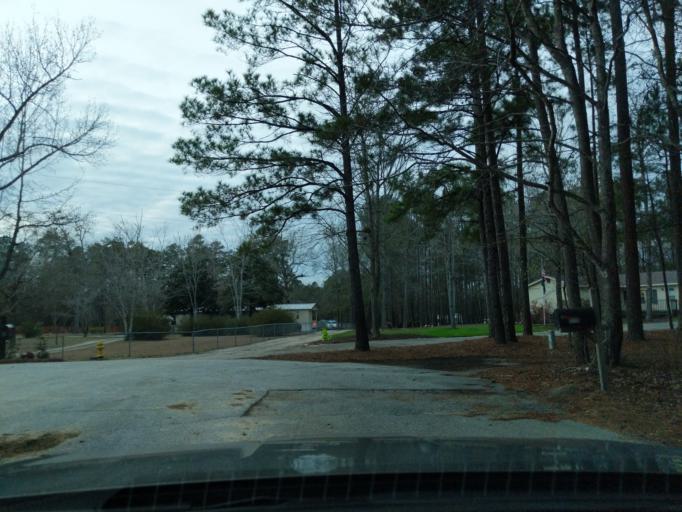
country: US
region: Georgia
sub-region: Columbia County
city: Grovetown
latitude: 33.4627
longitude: -82.1979
